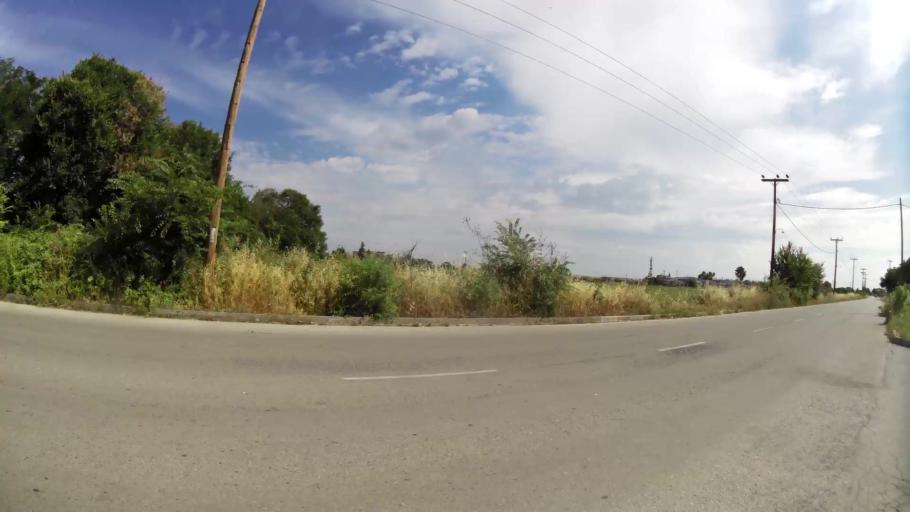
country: GR
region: Central Macedonia
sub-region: Nomos Pierias
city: Katerini
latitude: 40.2844
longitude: 22.4996
